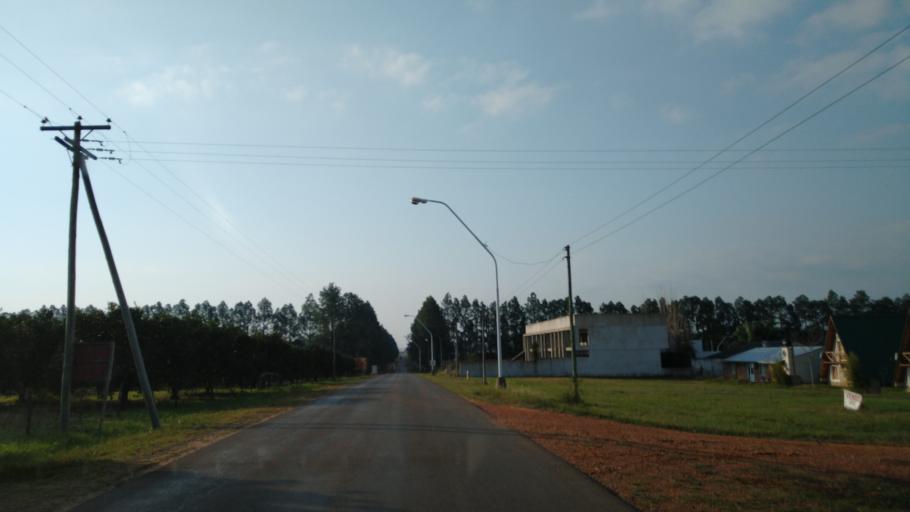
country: AR
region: Entre Rios
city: Santa Ana
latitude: -30.9106
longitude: -57.9264
